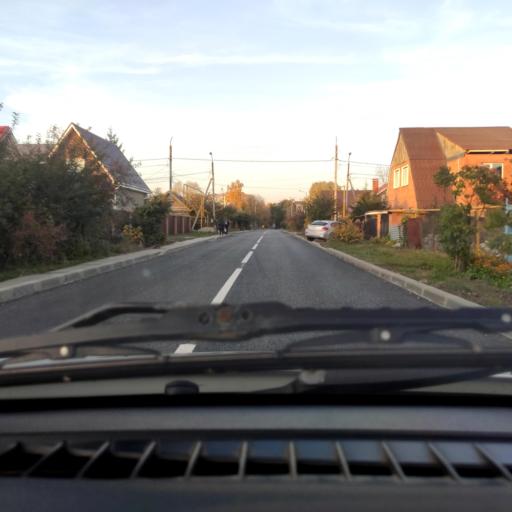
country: RU
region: Samara
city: Tol'yatti
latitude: 53.5286
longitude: 49.4211
